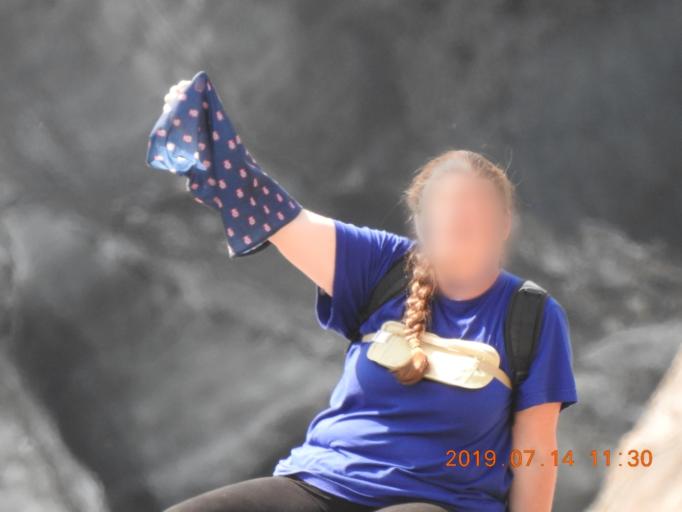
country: NO
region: Hordaland
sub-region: Odda
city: Odda
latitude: 60.0424
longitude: 6.4402
